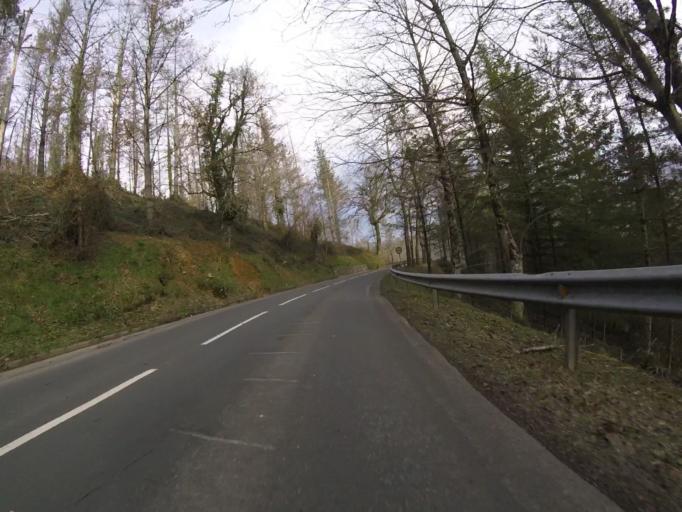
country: ES
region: Basque Country
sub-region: Provincia de Guipuzcoa
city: Beizama
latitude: 43.1590
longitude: -2.2076
